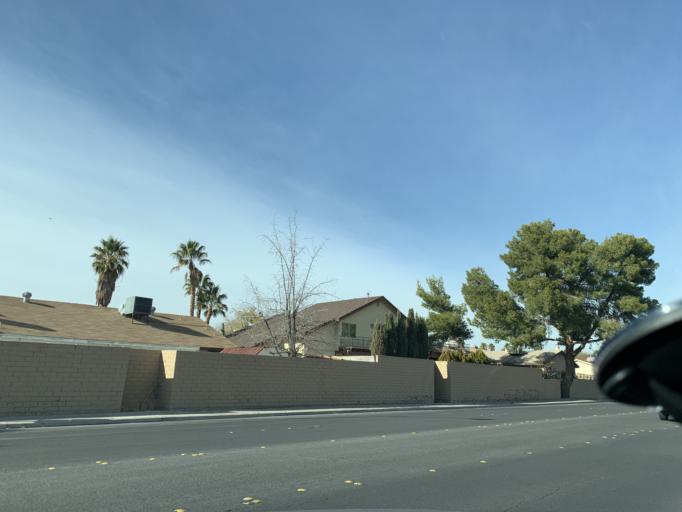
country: US
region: Nevada
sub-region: Clark County
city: Spring Valley
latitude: 36.1085
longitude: -115.2339
